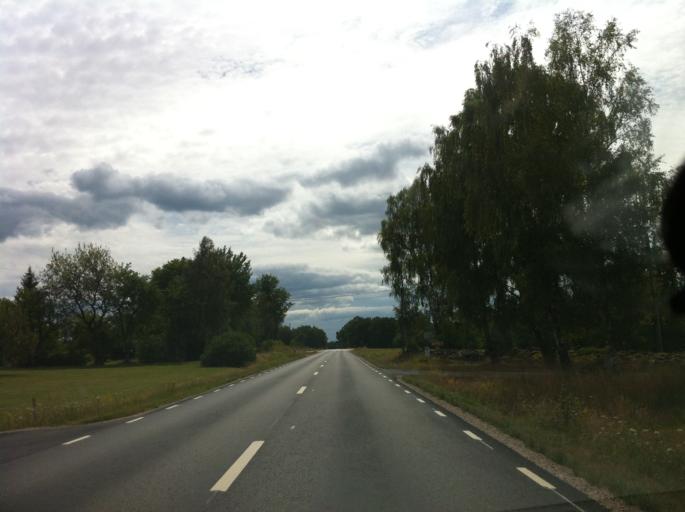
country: SE
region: Kronoberg
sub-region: Tingsryds Kommun
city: Tingsryd
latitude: 56.5356
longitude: 15.1760
